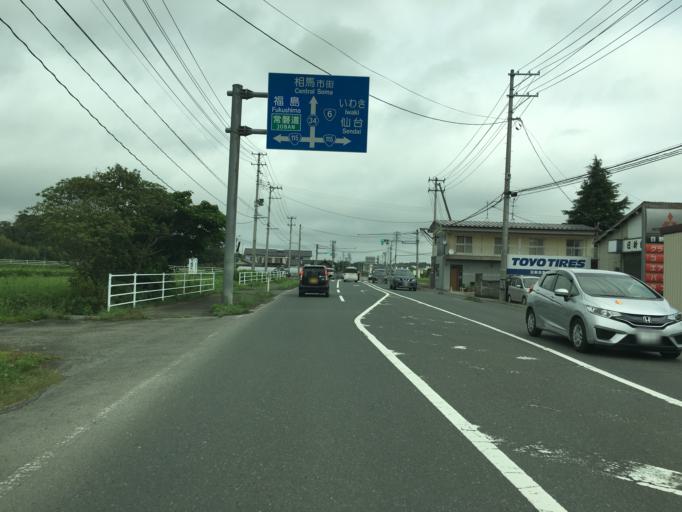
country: JP
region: Miyagi
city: Marumori
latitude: 37.7846
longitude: 140.9142
